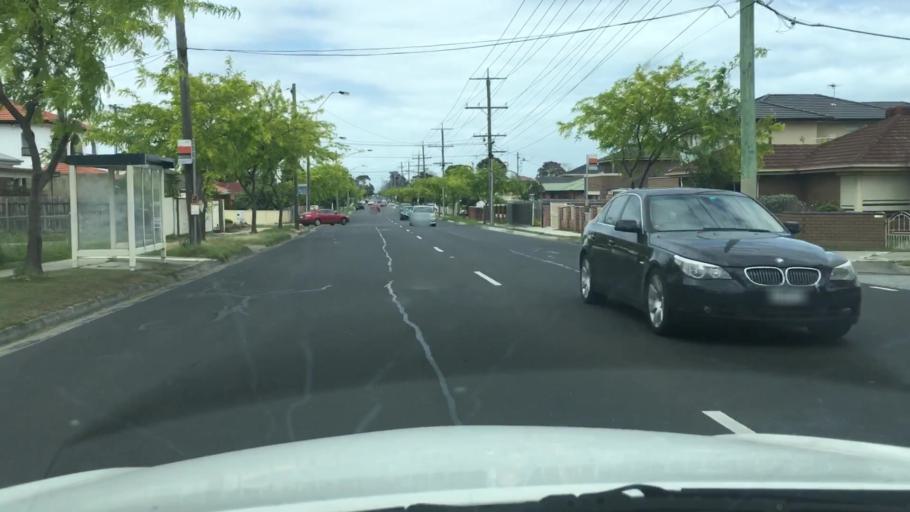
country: AU
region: Victoria
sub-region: Greater Dandenong
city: Noble Park
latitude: -37.9756
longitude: 145.1663
